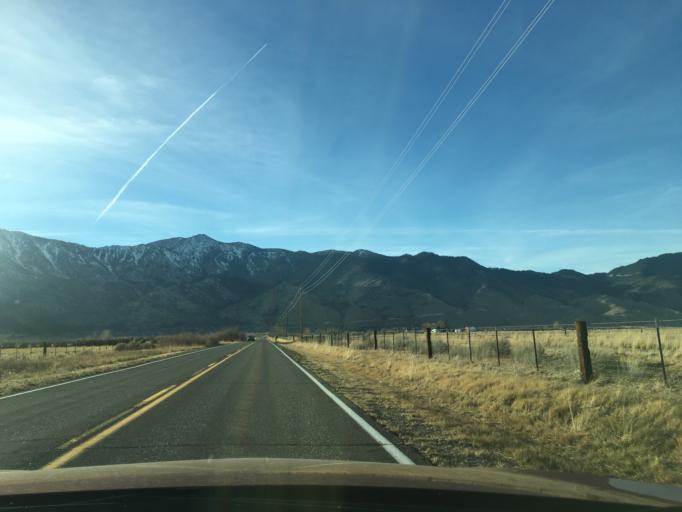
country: US
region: Nevada
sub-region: Douglas County
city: Minden
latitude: 38.9322
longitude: -119.7893
